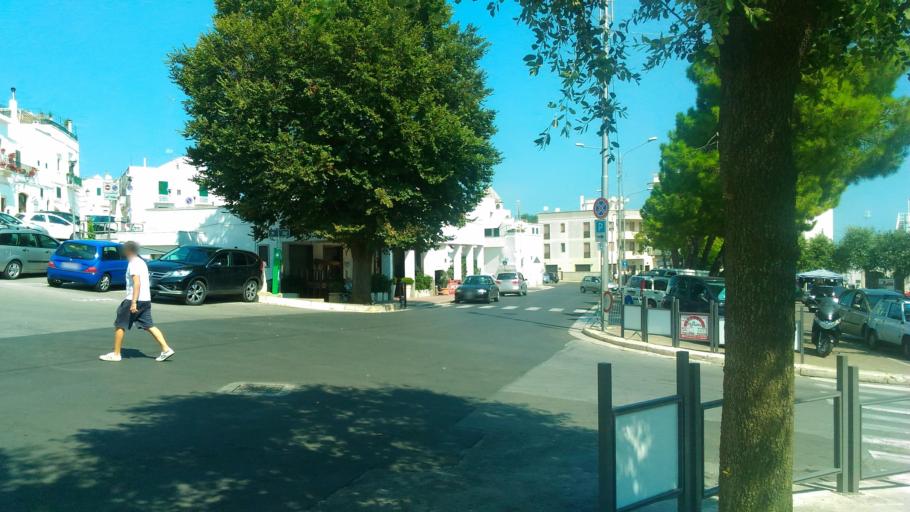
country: IT
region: Apulia
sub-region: Provincia di Bari
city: Locorotondo
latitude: 40.7528
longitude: 17.3307
